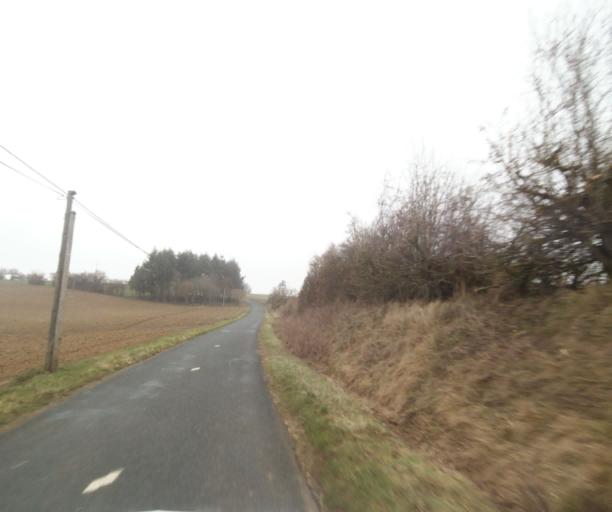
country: FR
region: Champagne-Ardenne
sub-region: Departement de la Haute-Marne
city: Wassy
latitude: 48.5112
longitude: 5.0145
